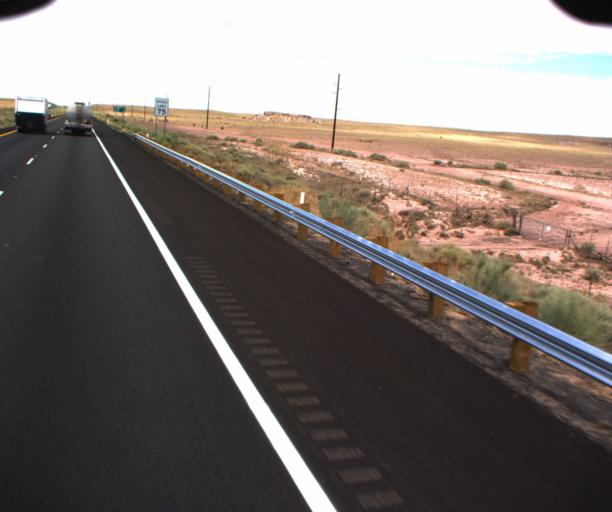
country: US
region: Arizona
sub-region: Navajo County
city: Holbrook
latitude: 34.9986
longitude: -109.9123
